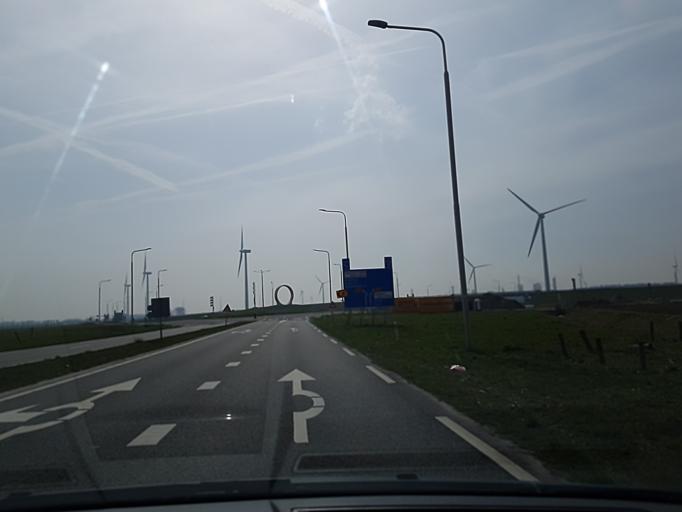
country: NL
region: Zeeland
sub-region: Gemeente Terneuzen
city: Sluiskil
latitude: 51.2970
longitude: 3.8631
